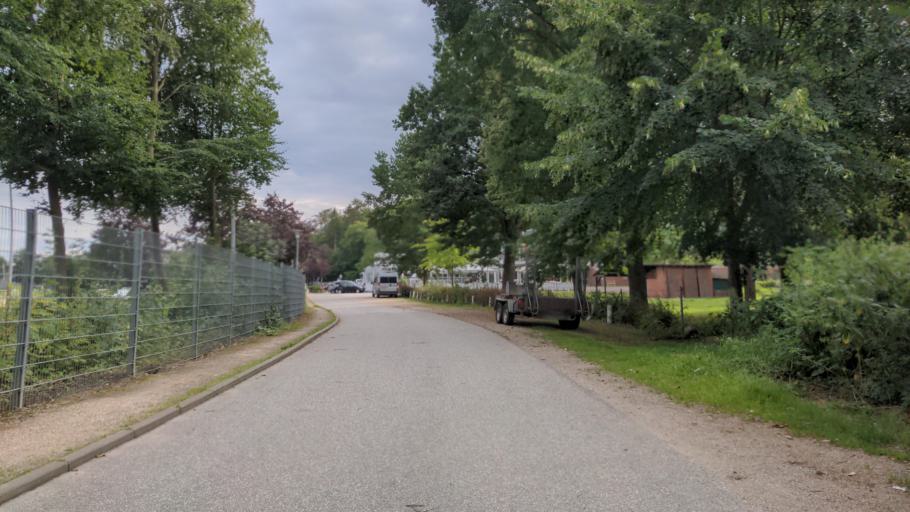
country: DE
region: Schleswig-Holstein
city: Neustadt in Holstein
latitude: 54.1086
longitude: 10.8048
